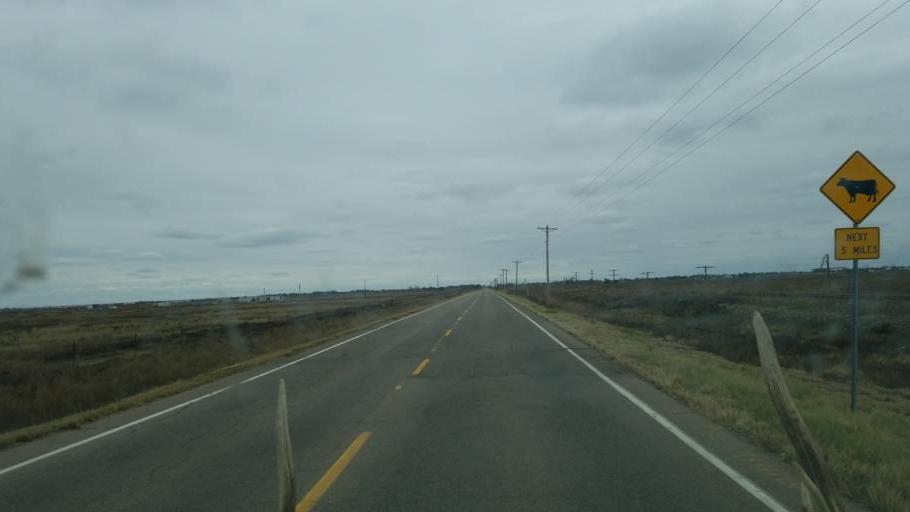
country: US
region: Colorado
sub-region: Crowley County
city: Ordway
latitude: 38.2260
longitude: -103.7049
